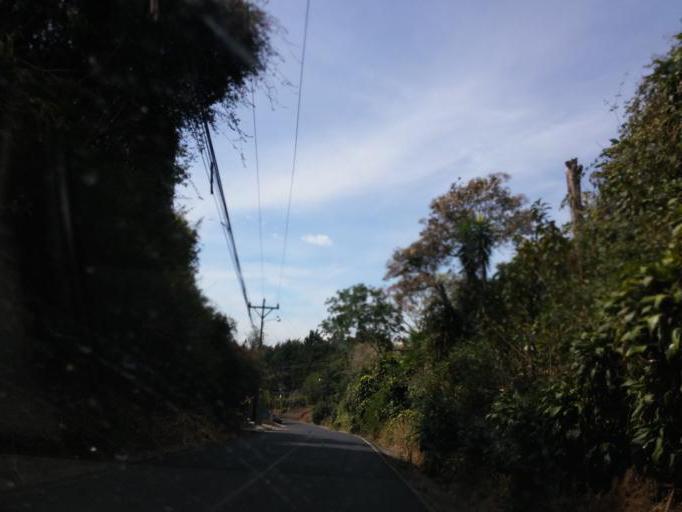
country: CR
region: Alajuela
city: Sabanilla
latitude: 10.0533
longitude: -84.2162
